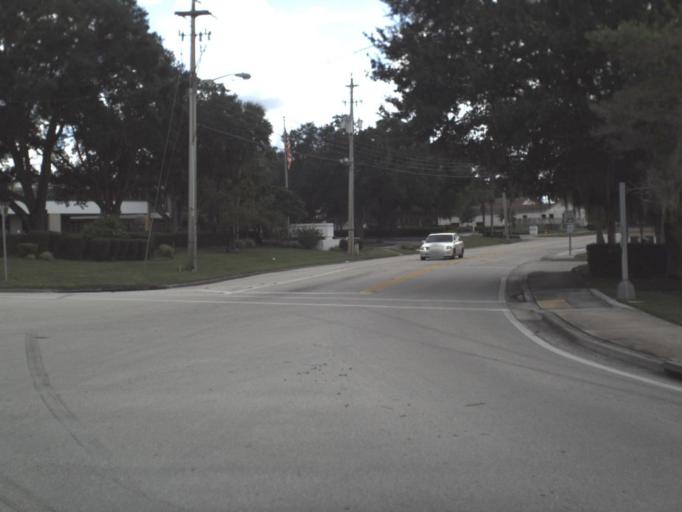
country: US
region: Florida
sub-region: Polk County
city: Winter Haven
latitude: 28.0295
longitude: -81.7268
